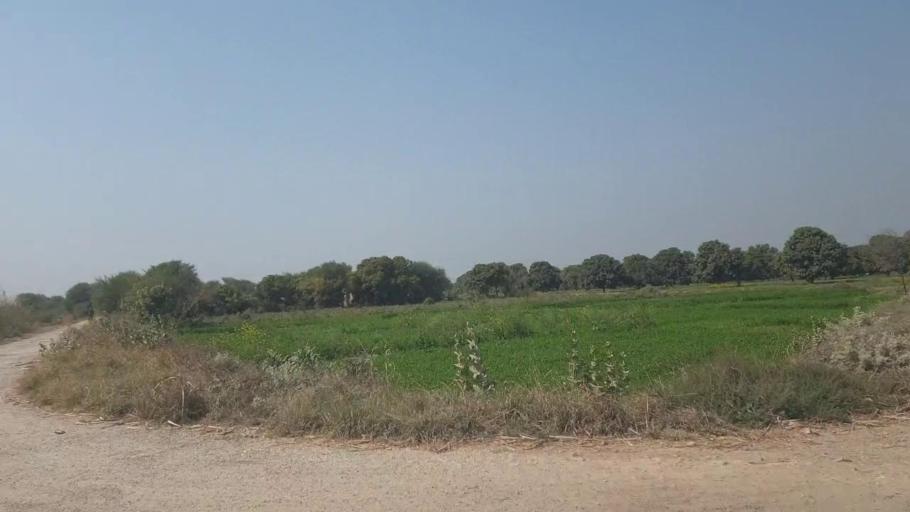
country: PK
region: Sindh
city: Tando Allahyar
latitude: 25.4795
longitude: 68.8037
